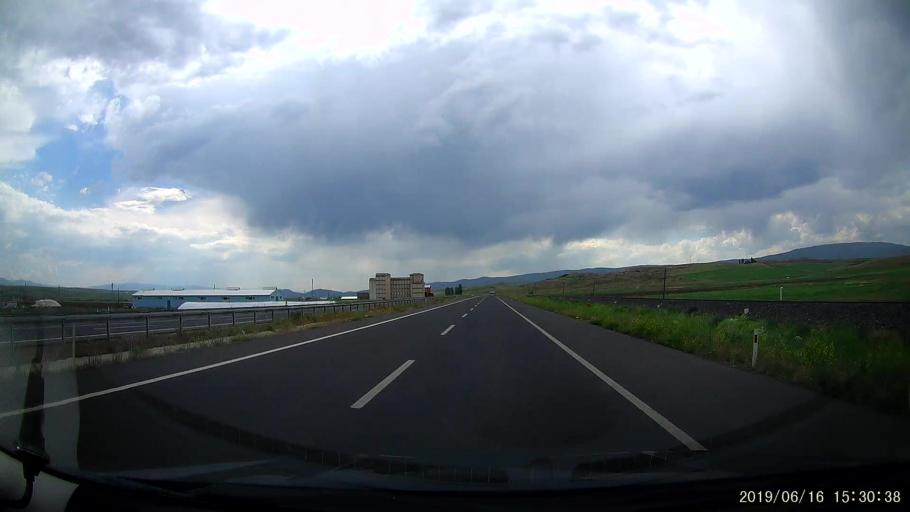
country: TR
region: Erzurum
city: Horasan
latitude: 40.0341
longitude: 42.0996
